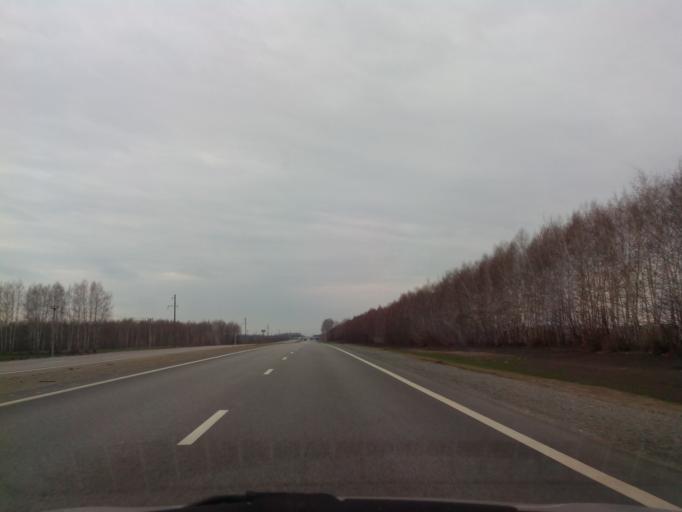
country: RU
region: Tambov
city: Zavoronezhskoye
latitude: 52.8810
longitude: 40.7349
